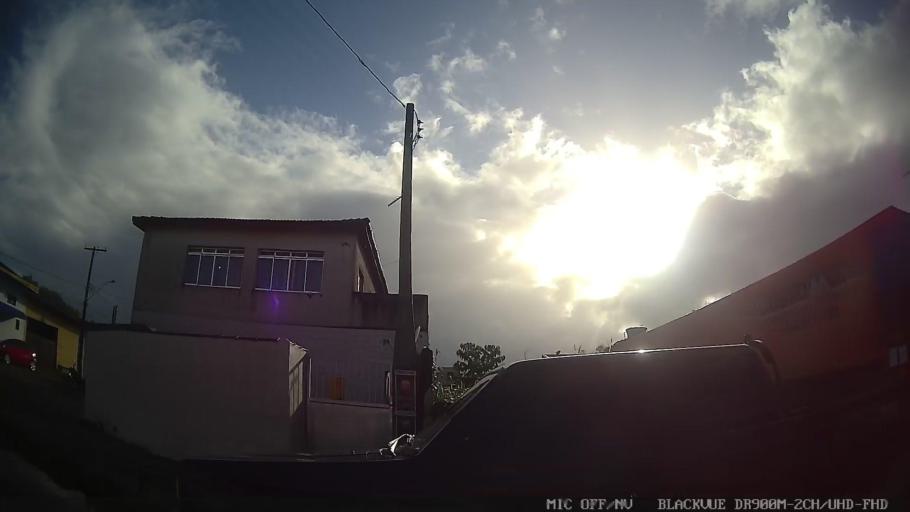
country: BR
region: Sao Paulo
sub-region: Itanhaem
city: Itanhaem
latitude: -24.2369
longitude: -46.8993
